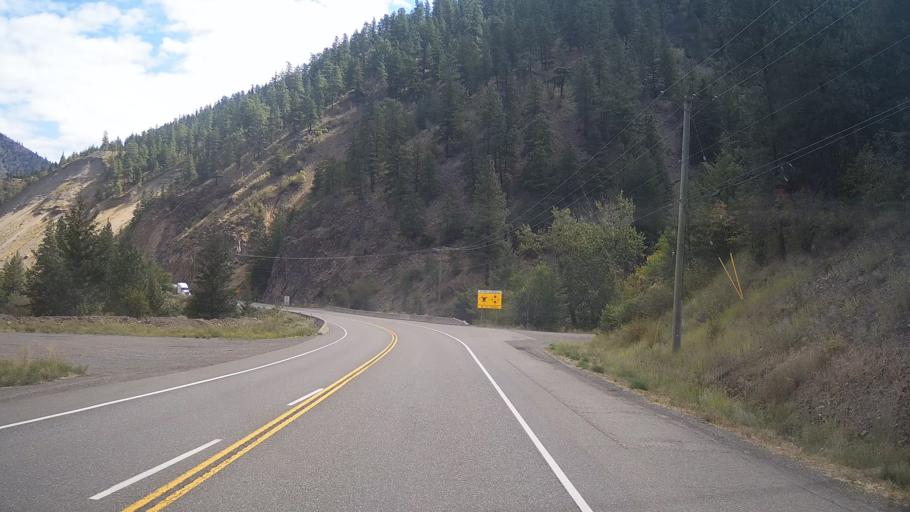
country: CA
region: British Columbia
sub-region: Thompson-Nicola Regional District
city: Ashcroft
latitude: 50.2479
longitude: -121.4794
